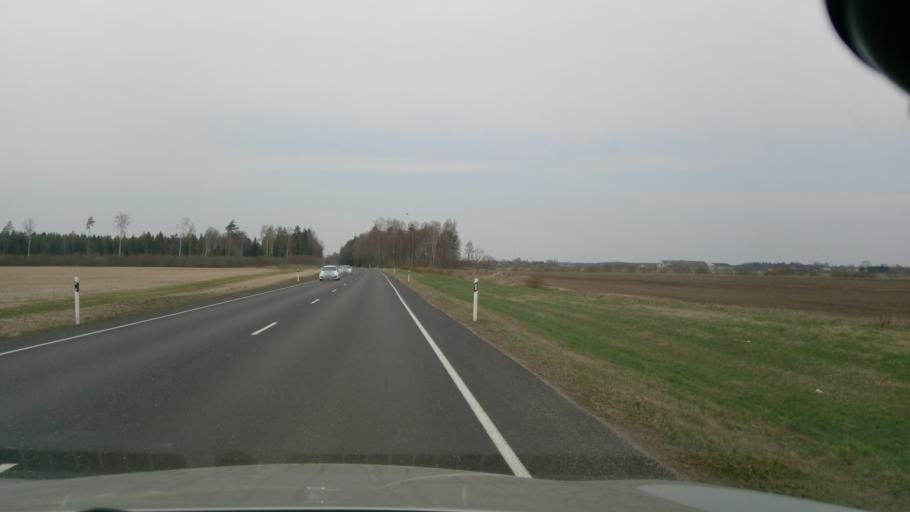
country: EE
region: Viljandimaa
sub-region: Vohma linn
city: Vohma
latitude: 58.7365
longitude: 25.5878
